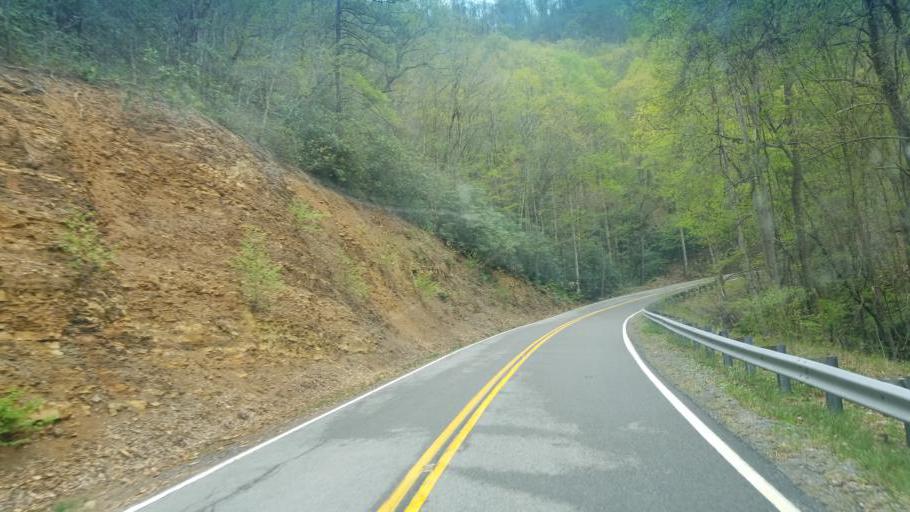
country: US
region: Virginia
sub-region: Tazewell County
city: Tazewell
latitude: 37.0048
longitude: -81.5187
